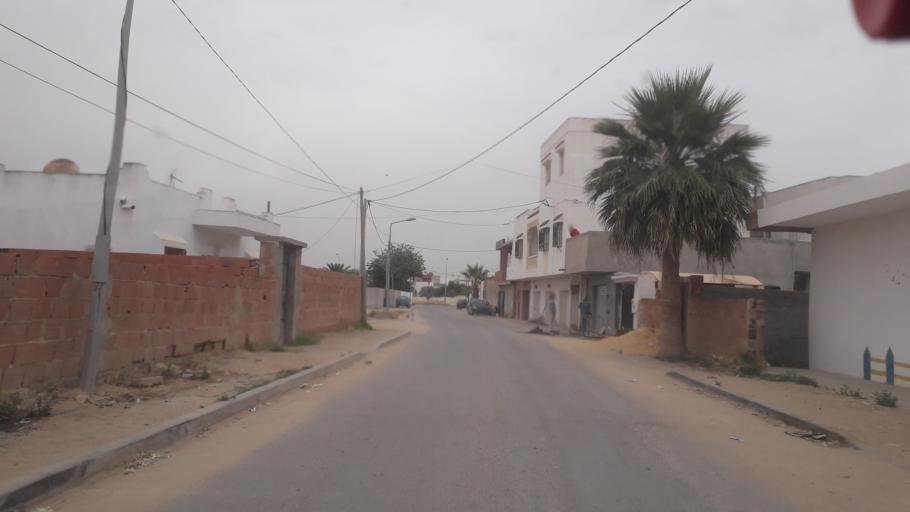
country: TN
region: Safaqis
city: Al Qarmadah
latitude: 34.7911
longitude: 10.7680
